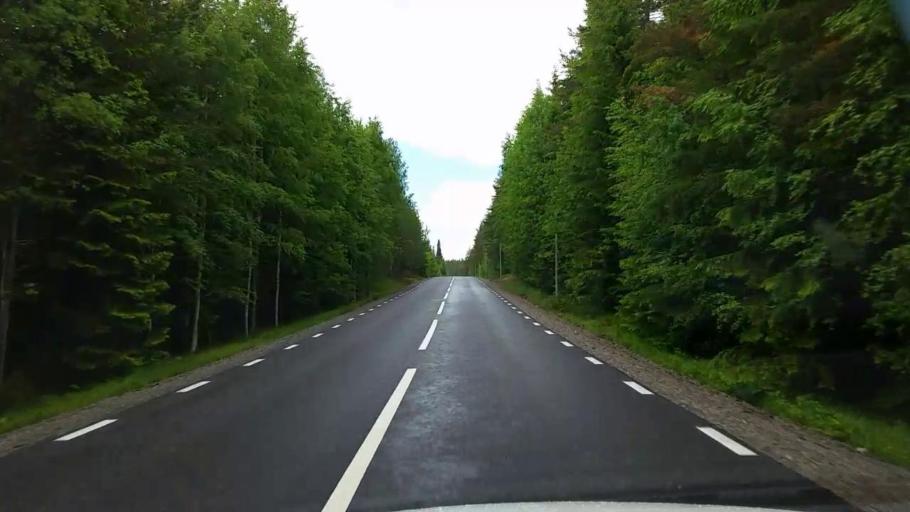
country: SE
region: Gaevleborg
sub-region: Sandvikens Kommun
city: Jarbo
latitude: 60.8588
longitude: 16.4378
